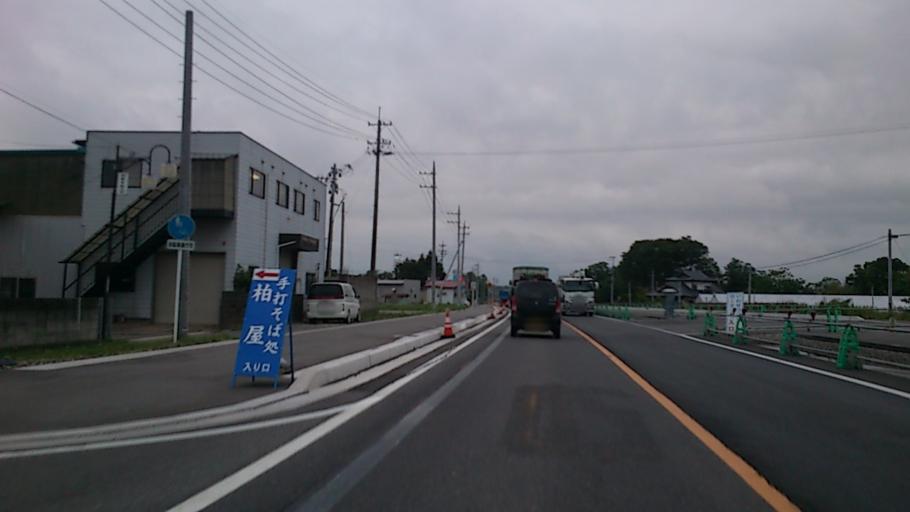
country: JP
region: Fukushima
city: Sukagawa
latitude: 37.2628
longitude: 140.3499
